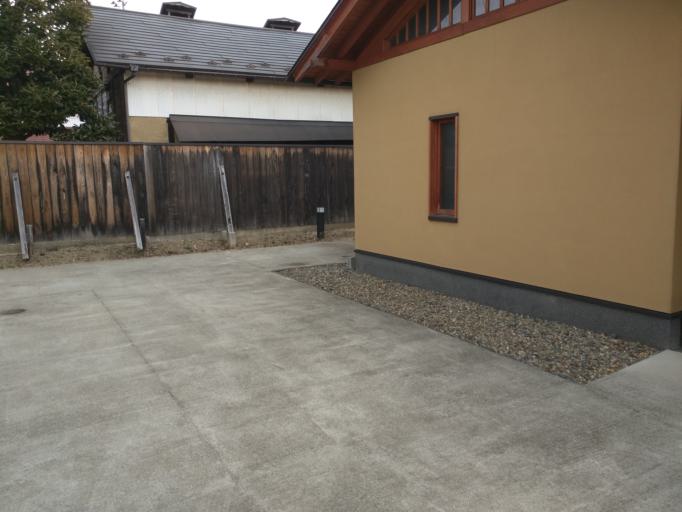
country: JP
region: Fukushima
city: Fukushima-shi
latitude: 37.8334
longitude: 140.4525
